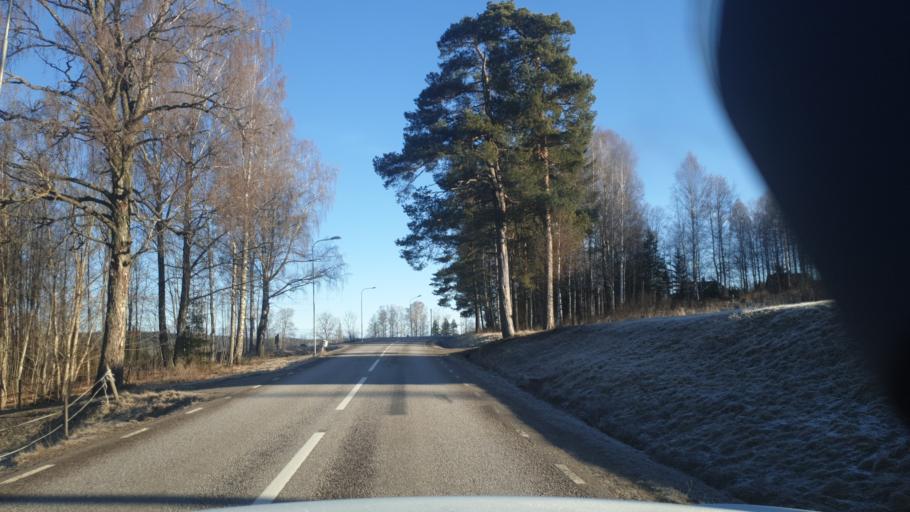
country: SE
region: Vaermland
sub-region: Eda Kommun
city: Amotfors
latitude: 59.6843
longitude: 12.1479
